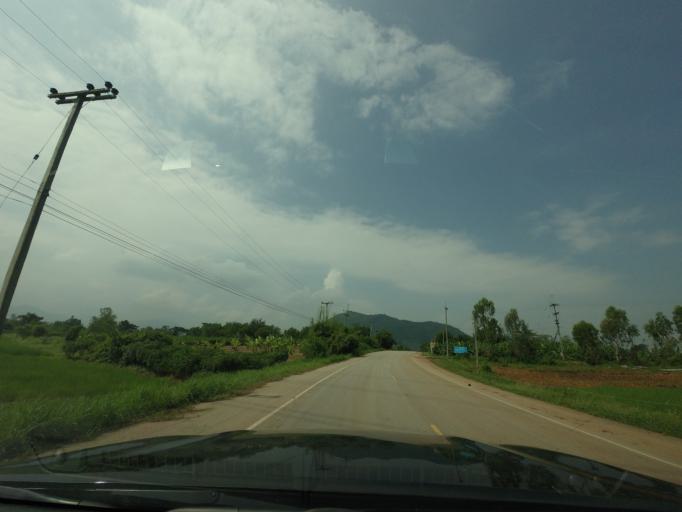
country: LA
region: Xiagnabouli
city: Muang Kenthao
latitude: 17.6812
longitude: 101.4077
